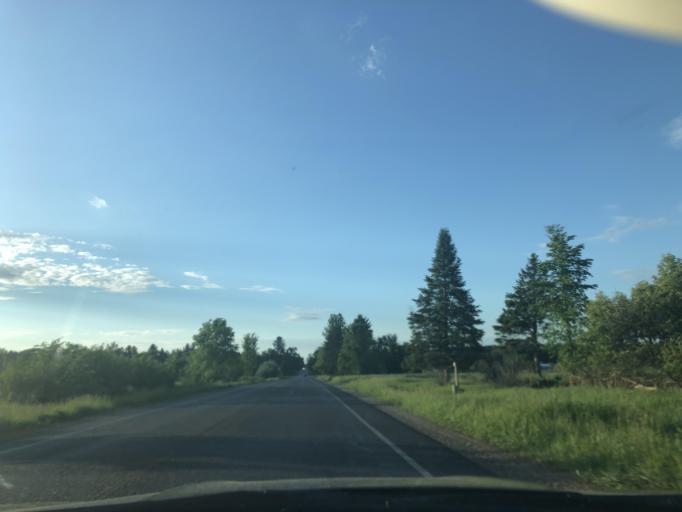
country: US
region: Michigan
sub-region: Missaukee County
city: Lake City
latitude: 44.3429
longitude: -85.0755
